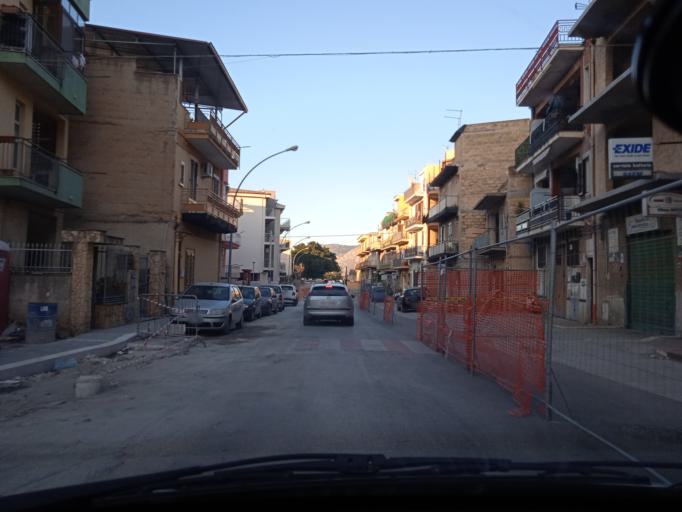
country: IT
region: Sicily
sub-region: Palermo
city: Ficarazzi
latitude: 38.0898
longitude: 13.4729
